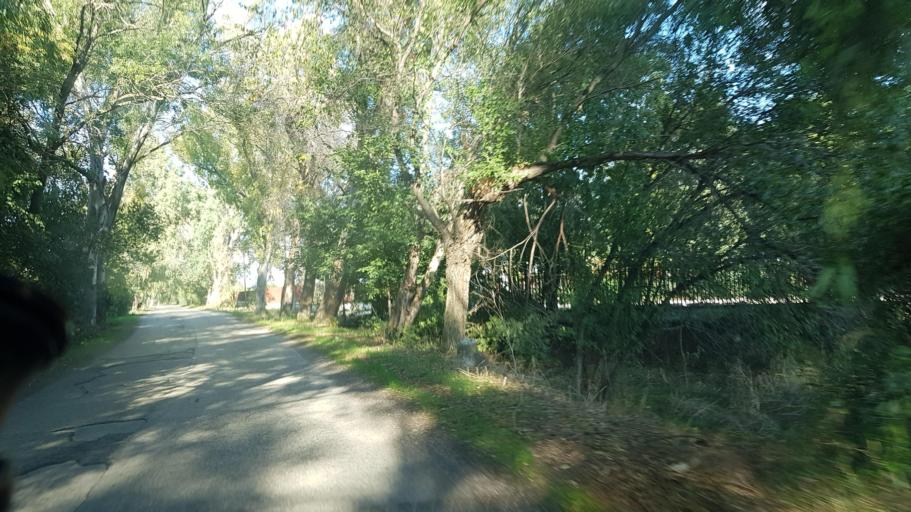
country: IT
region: Apulia
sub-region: Provincia di Foggia
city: Carapelle
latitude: 41.3951
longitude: 15.6522
